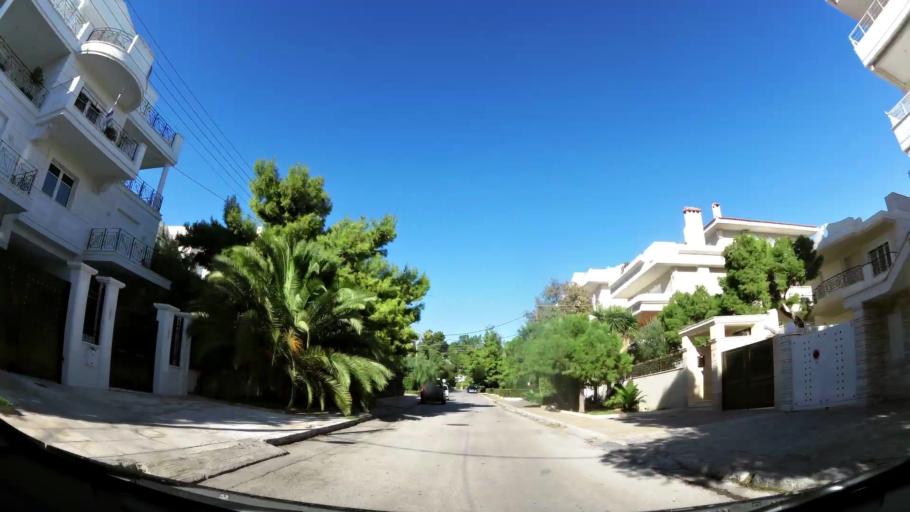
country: GR
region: Attica
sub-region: Nomarchia Anatolikis Attikis
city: Voula
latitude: 37.8445
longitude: 23.7659
